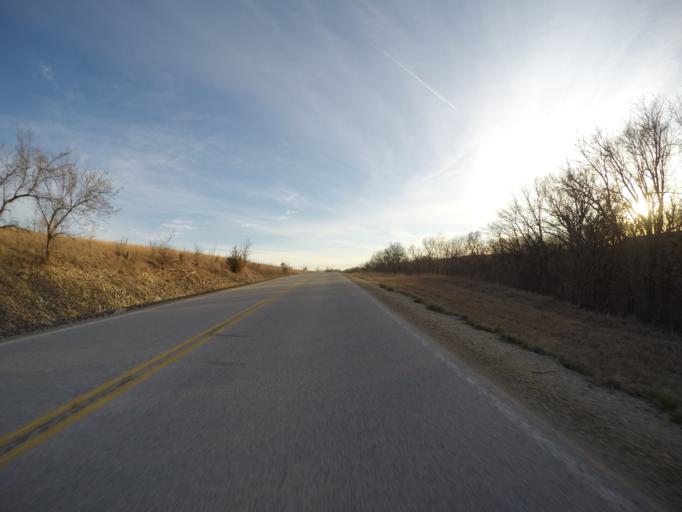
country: US
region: Kansas
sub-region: Riley County
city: Ogden
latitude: 39.3071
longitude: -96.7454
